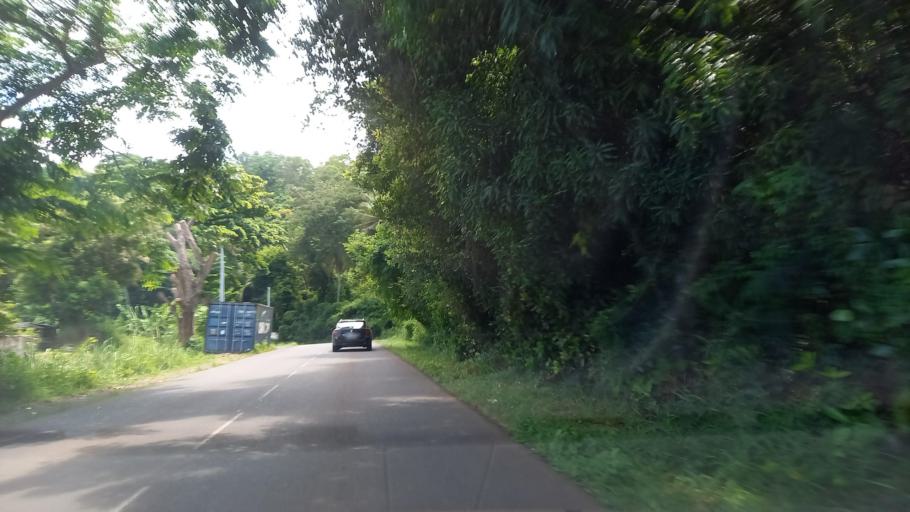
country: YT
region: Sada
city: Sada
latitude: -12.8538
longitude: 45.1047
